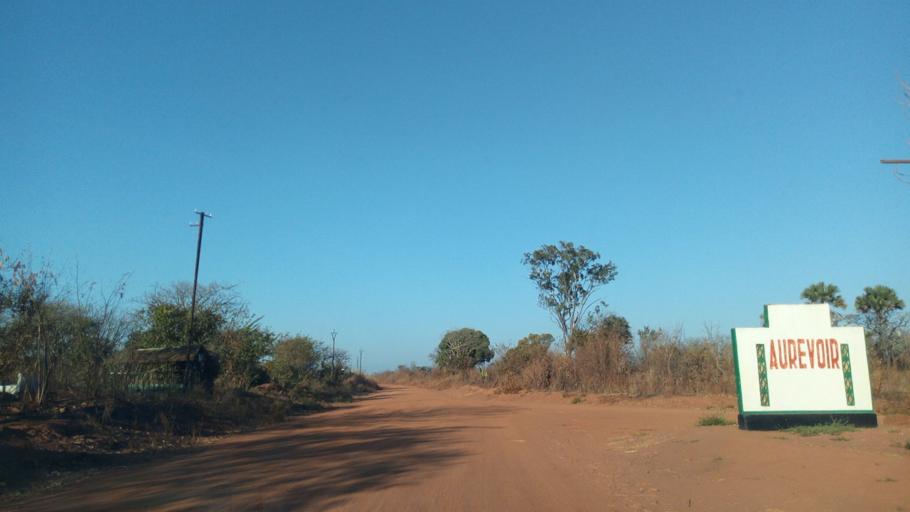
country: ZM
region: Luapula
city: Mwense
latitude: -10.4114
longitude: 28.6100
